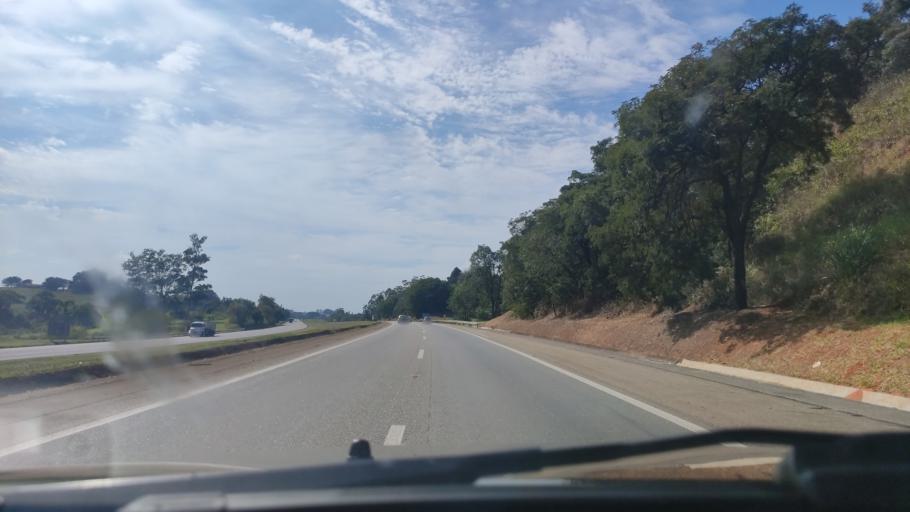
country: BR
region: Sao Paulo
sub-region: Boituva
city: Boituva
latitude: -23.2958
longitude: -47.7117
